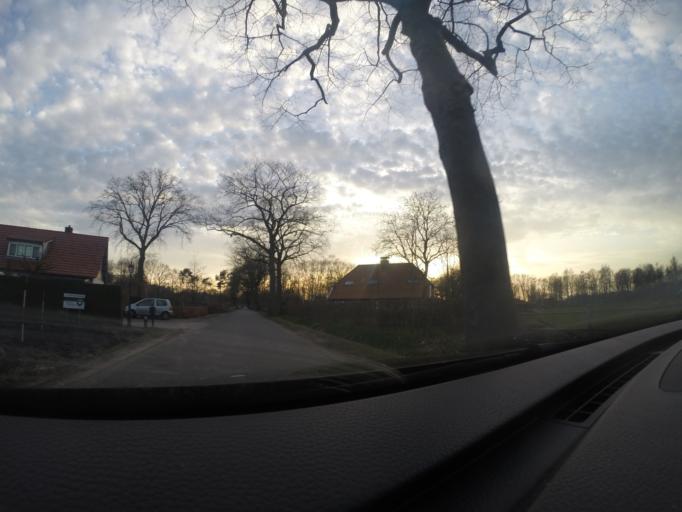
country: NL
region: Overijssel
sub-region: Gemeente Haaksbergen
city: Haaksbergen
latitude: 52.1422
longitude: 6.7362
